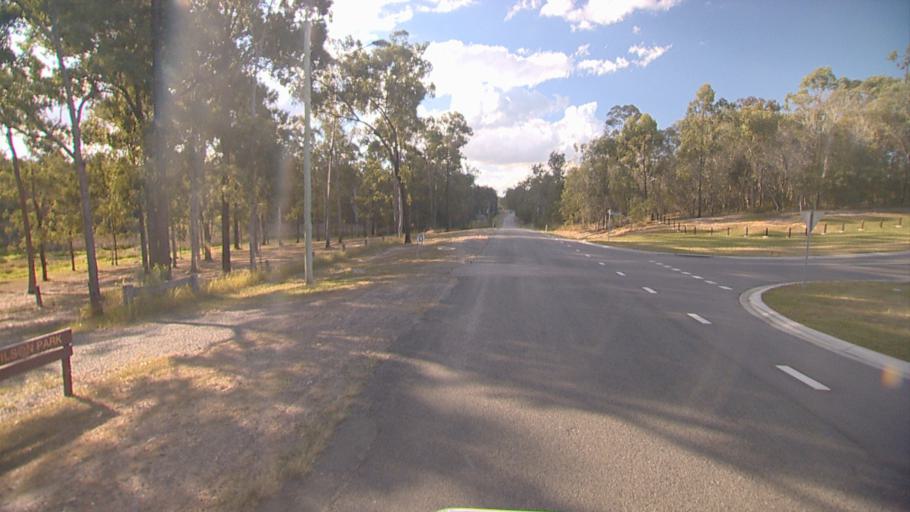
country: AU
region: Queensland
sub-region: Logan
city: North Maclean
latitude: -27.7456
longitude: 152.9410
